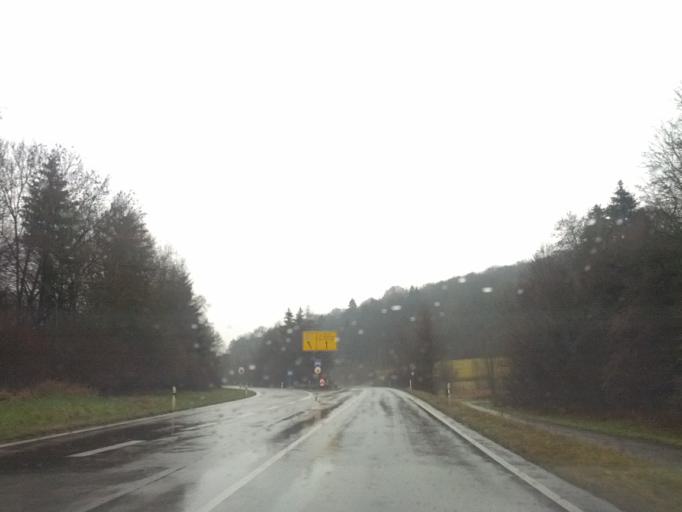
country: DE
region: Baden-Wuerttemberg
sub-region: Tuebingen Region
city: Ummendorf
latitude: 48.0764
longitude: 9.8168
